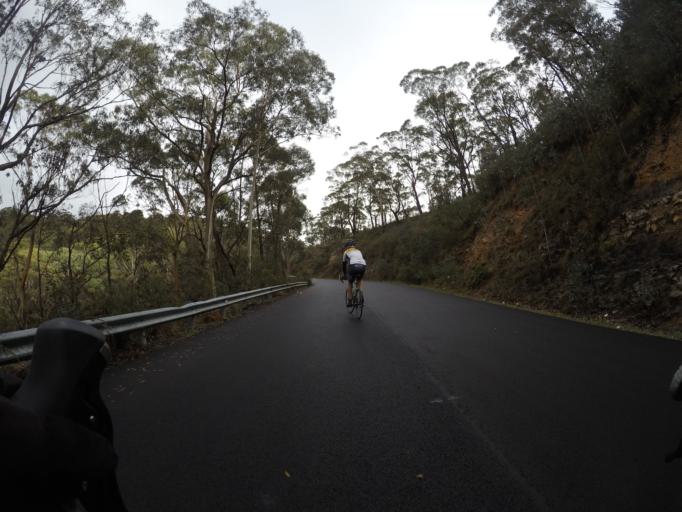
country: AU
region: New South Wales
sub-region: Lithgow
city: Lithgow
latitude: -33.5022
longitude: 150.1725
